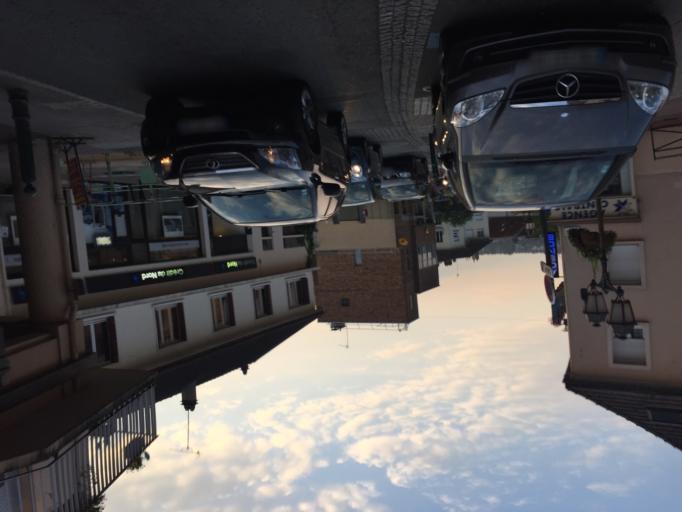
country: FR
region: Ile-de-France
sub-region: Departement de l'Essonne
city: Orsay
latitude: 48.6972
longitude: 2.1873
